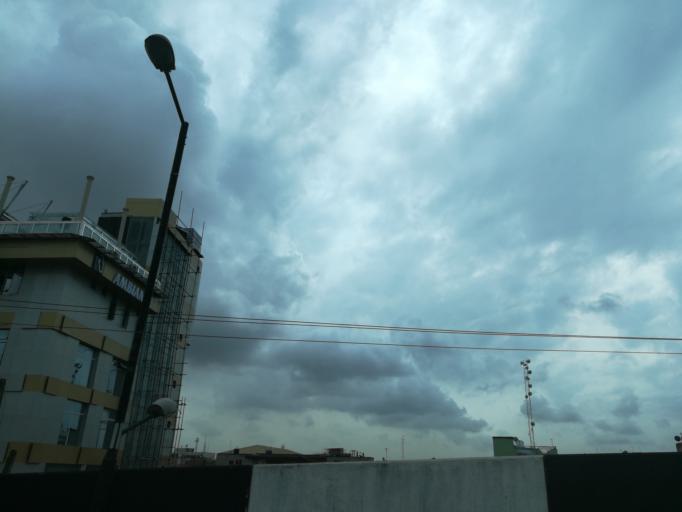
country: NG
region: Lagos
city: Ikeja
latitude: 6.5980
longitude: 3.3404
